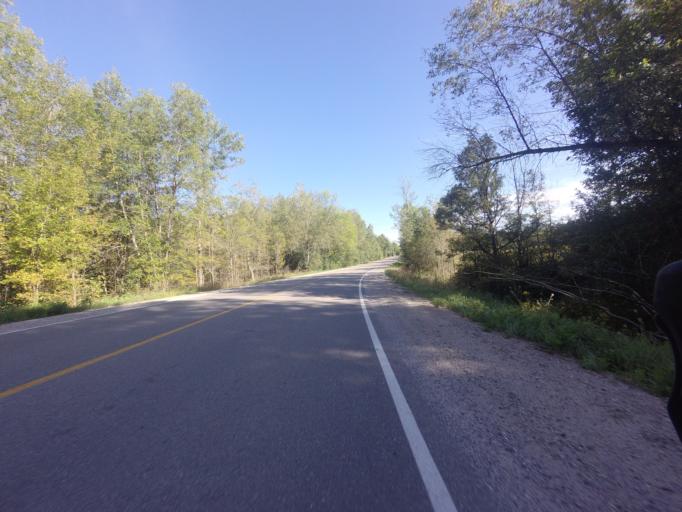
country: CA
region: Ontario
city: Perth
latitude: 44.9089
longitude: -76.3411
